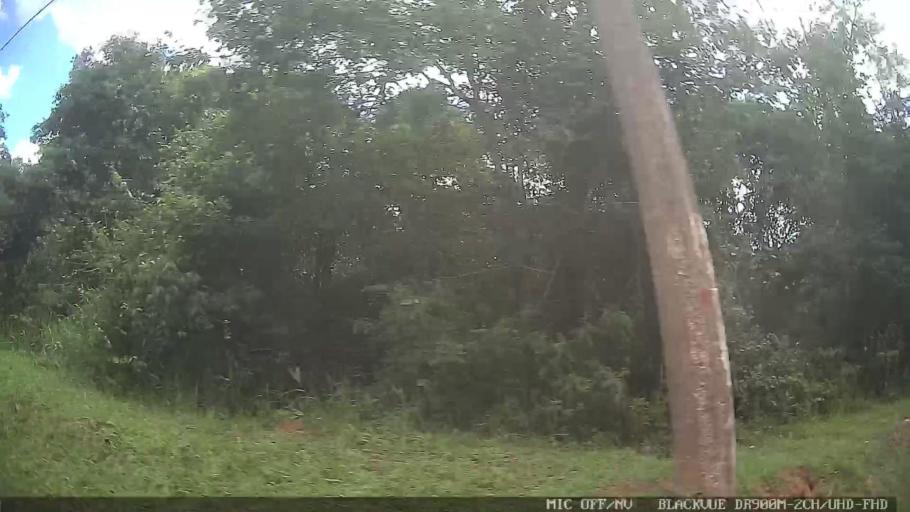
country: BR
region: Sao Paulo
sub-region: Atibaia
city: Atibaia
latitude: -23.0761
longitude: -46.5190
